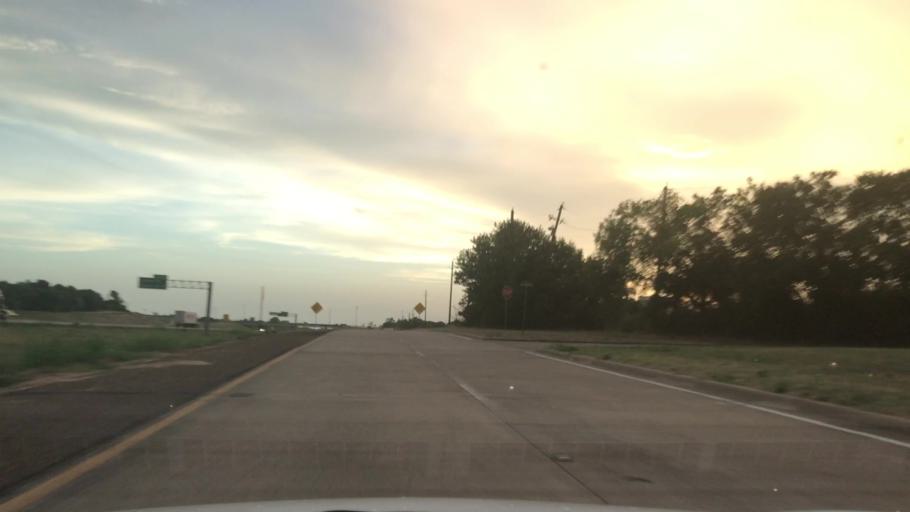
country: US
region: Texas
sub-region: Dallas County
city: Balch Springs
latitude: 32.7038
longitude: -96.5611
